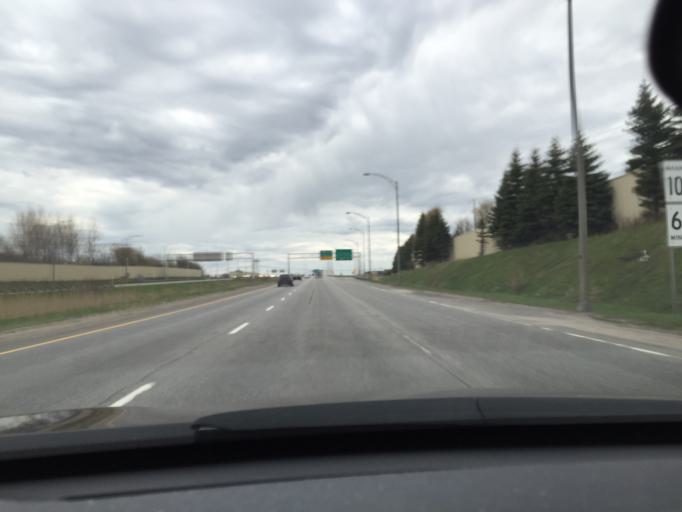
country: CA
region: Quebec
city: L'Ancienne-Lorette
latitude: 46.8185
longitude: -71.3206
